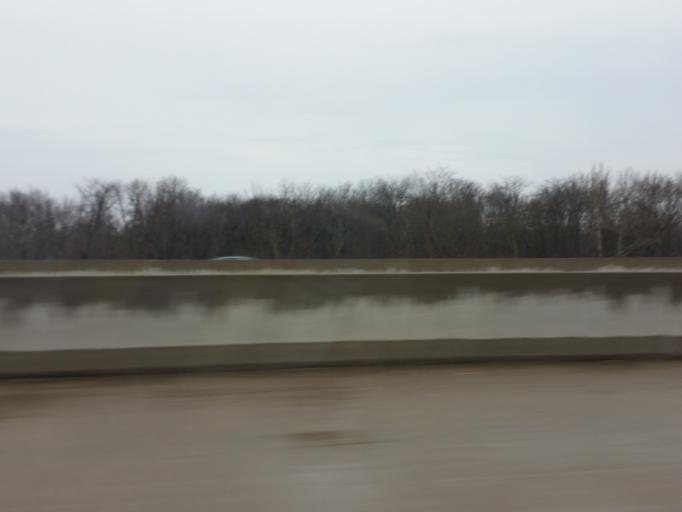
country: US
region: Iowa
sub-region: Cedar County
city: Tipton
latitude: 41.6457
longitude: -91.1350
